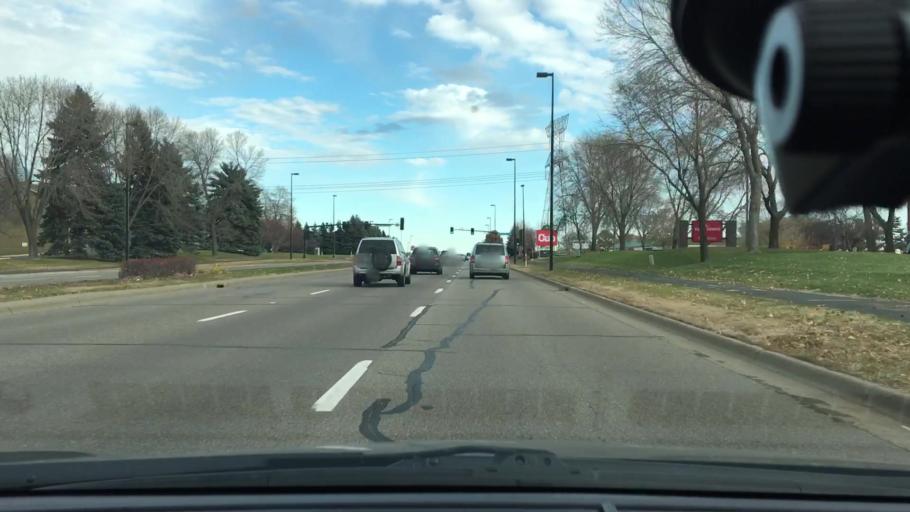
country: US
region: Minnesota
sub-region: Hennepin County
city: Maple Grove
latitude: 45.1047
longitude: -93.4499
